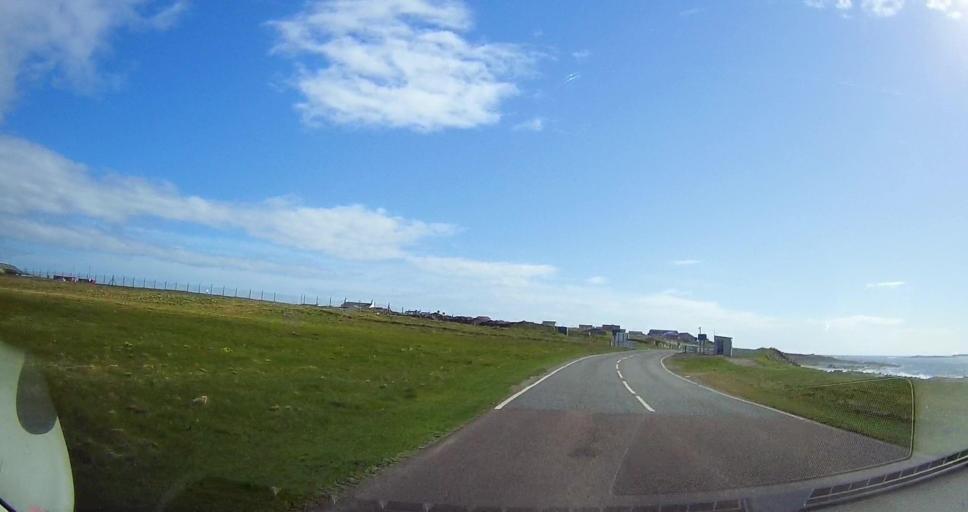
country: GB
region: Scotland
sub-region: Shetland Islands
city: Sandwick
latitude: 59.8808
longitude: -1.3054
